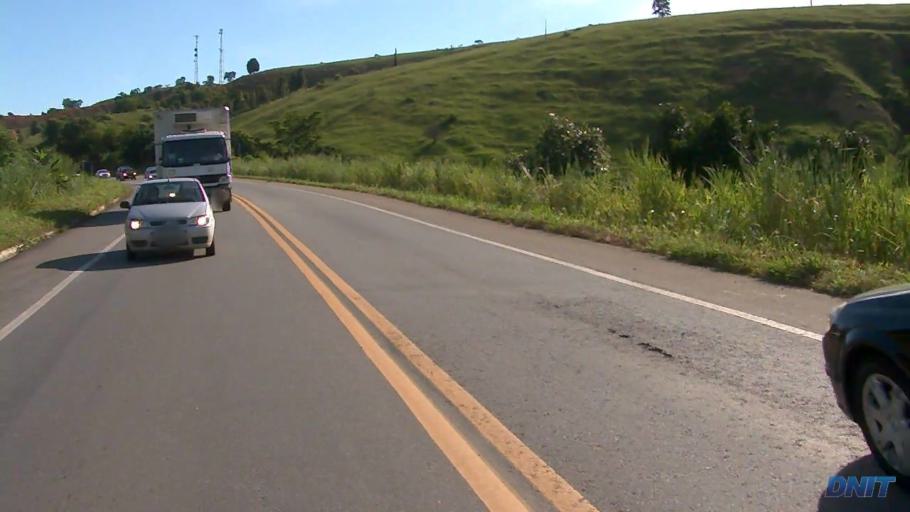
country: BR
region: Minas Gerais
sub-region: Belo Oriente
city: Belo Oriente
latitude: -19.2096
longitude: -42.3039
